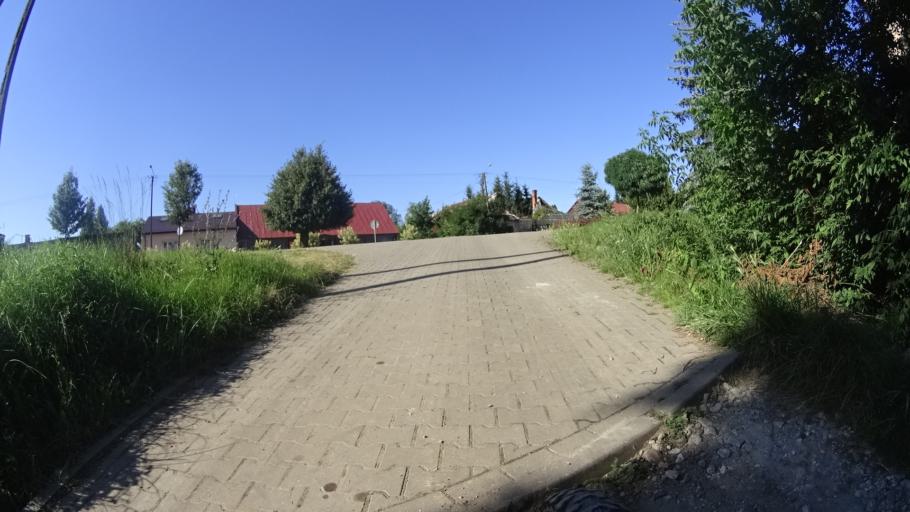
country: PL
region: Masovian Voivodeship
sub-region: Powiat bialobrzeski
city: Wysmierzyce
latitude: 51.6627
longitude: 20.8502
